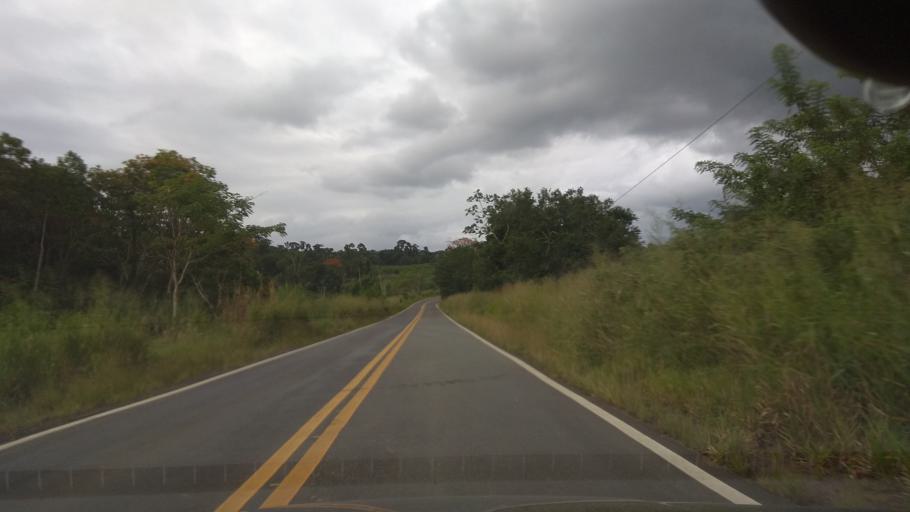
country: BR
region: Bahia
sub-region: Ubata
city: Ubata
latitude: -14.2052
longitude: -39.5750
